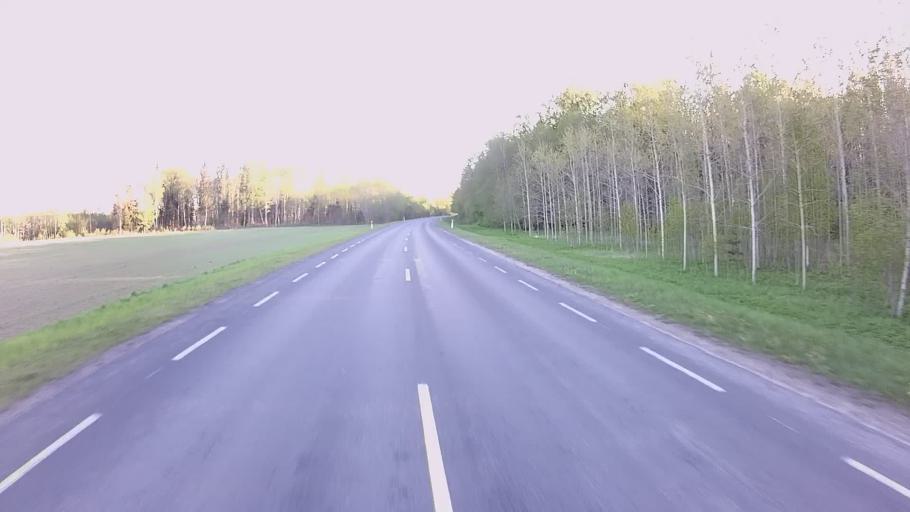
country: EE
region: Viljandimaa
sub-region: Viiratsi vald
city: Viiratsi
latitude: 58.4388
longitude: 25.7310
